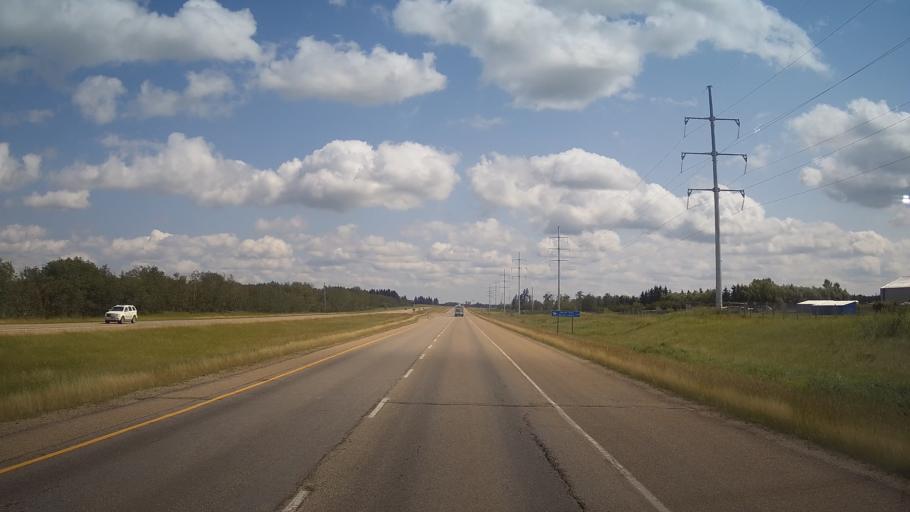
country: CA
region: Alberta
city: Sherwood Park
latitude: 53.4399
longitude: -113.2138
